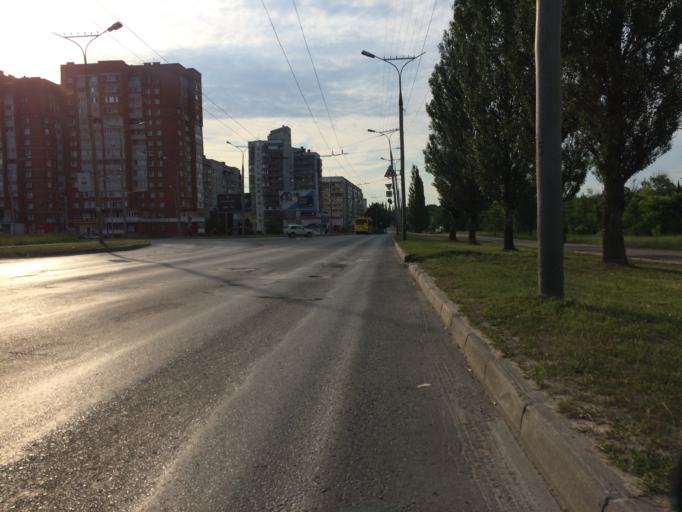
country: RU
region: Mariy-El
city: Yoshkar-Ola
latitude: 56.6239
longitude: 47.9320
